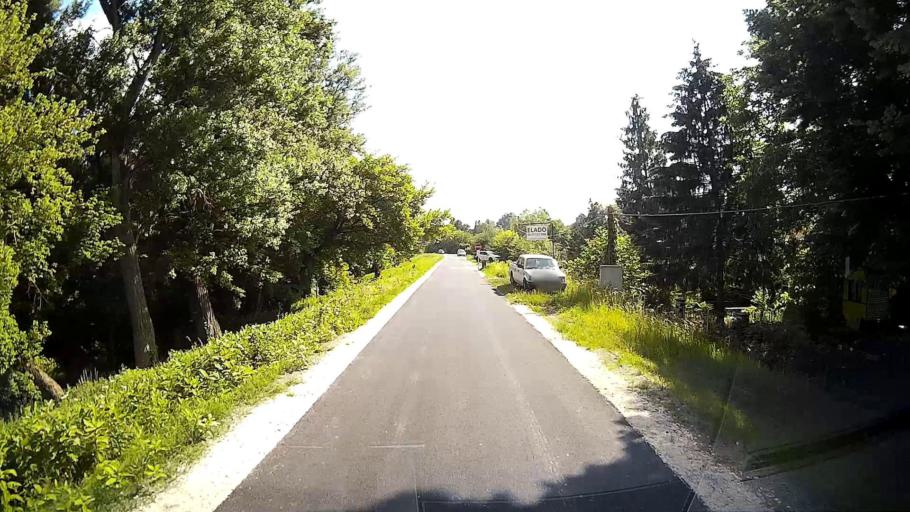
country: HU
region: Pest
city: God
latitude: 47.6700
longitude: 19.1139
